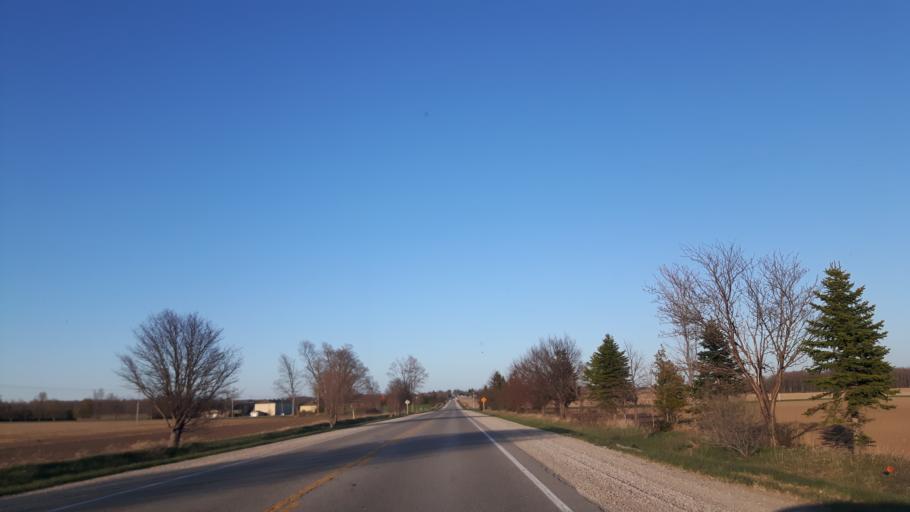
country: CA
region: Ontario
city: Bluewater
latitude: 43.5223
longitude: -81.5473
